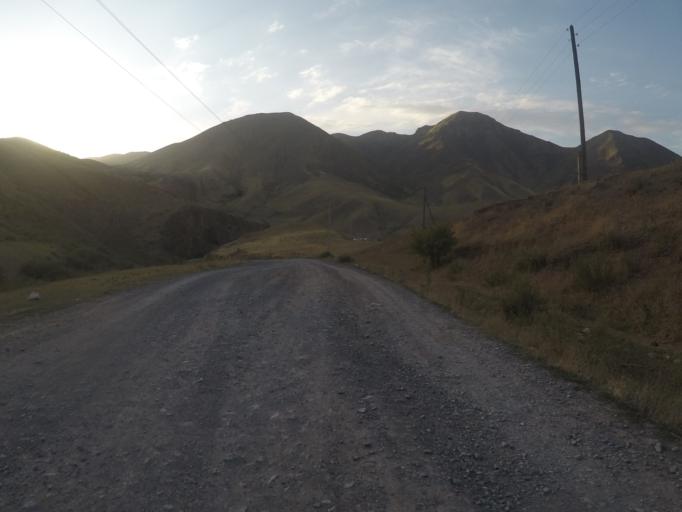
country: KG
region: Chuy
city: Bishkek
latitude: 42.6686
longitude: 74.6476
